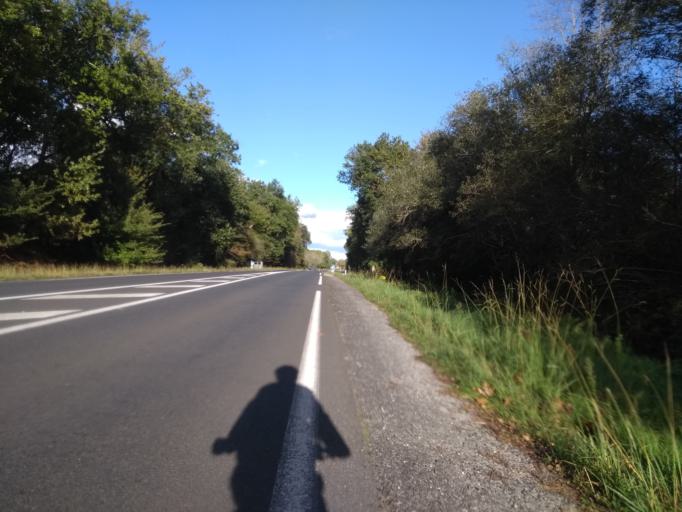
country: FR
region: Aquitaine
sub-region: Departement de la Gironde
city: Cestas
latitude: 44.7262
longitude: -0.6775
